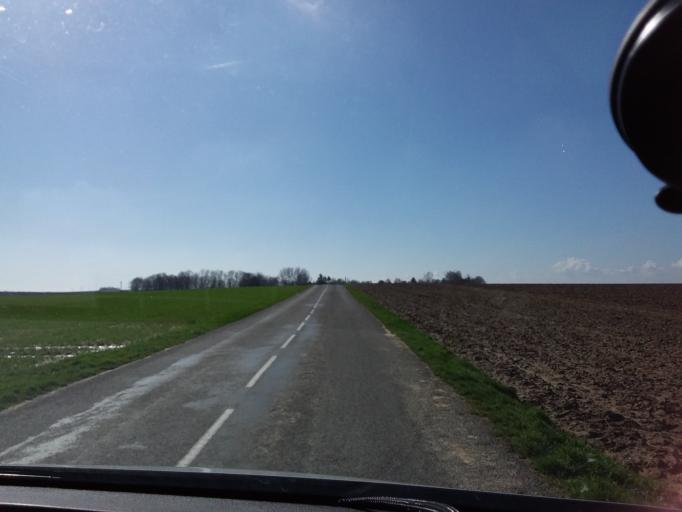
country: FR
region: Picardie
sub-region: Departement de l'Aisne
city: Montcornet
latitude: 49.7631
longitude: 4.0041
